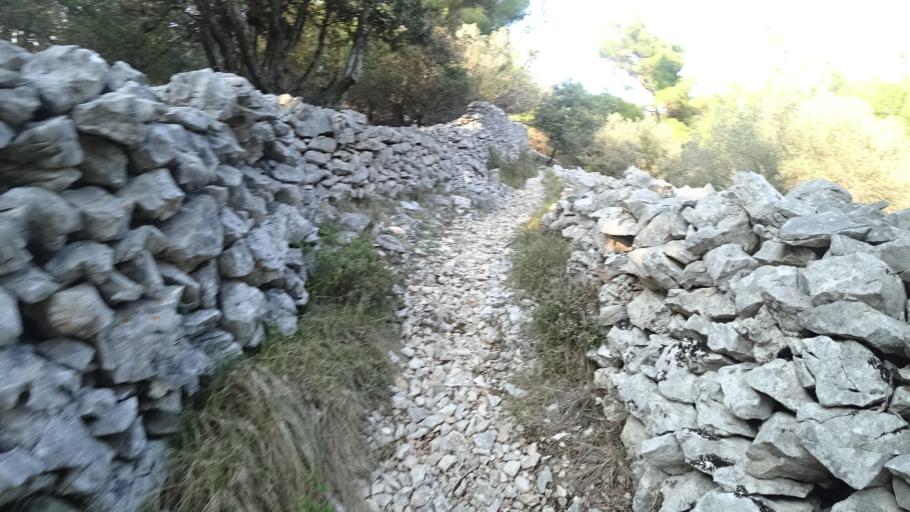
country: HR
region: Primorsko-Goranska
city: Mali Losinj
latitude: 44.5183
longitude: 14.4769
